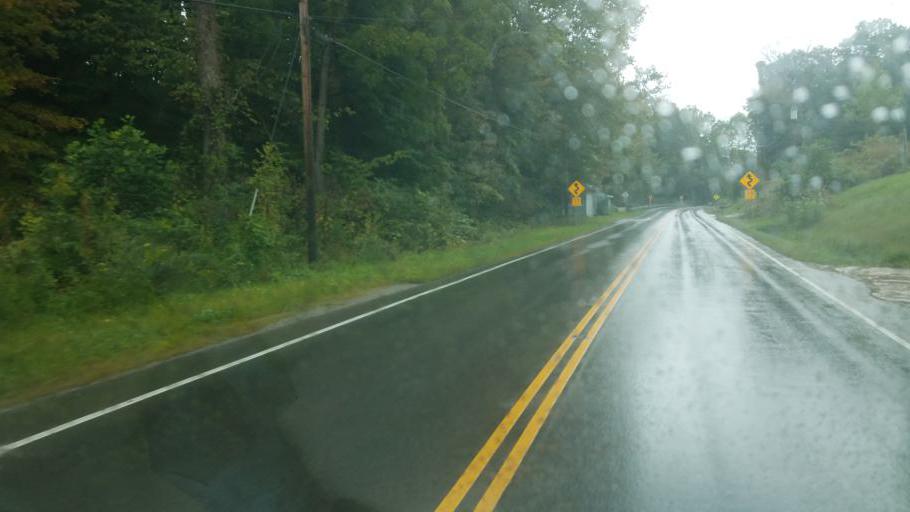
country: US
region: Ohio
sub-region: Scioto County
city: Wheelersburg
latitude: 38.7600
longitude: -82.8176
